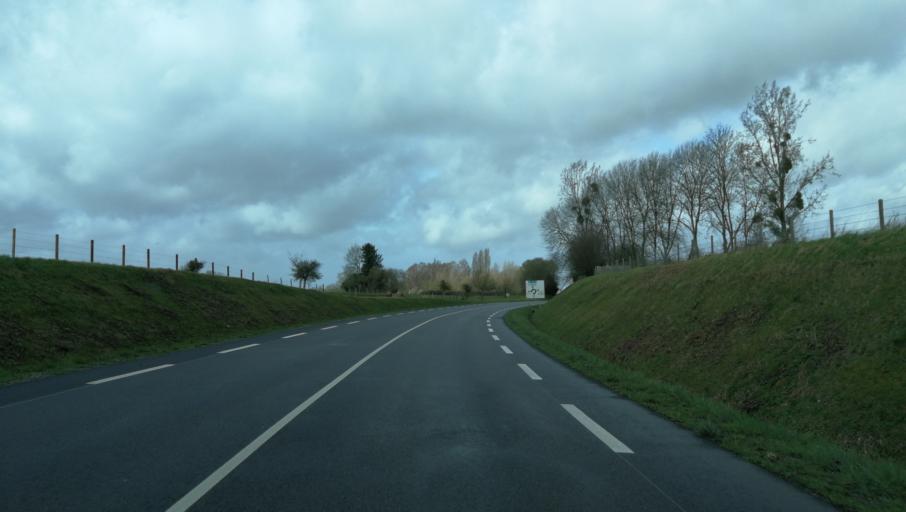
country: FR
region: Haute-Normandie
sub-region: Departement de l'Eure
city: Beuzeville
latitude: 49.3159
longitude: 0.3809
